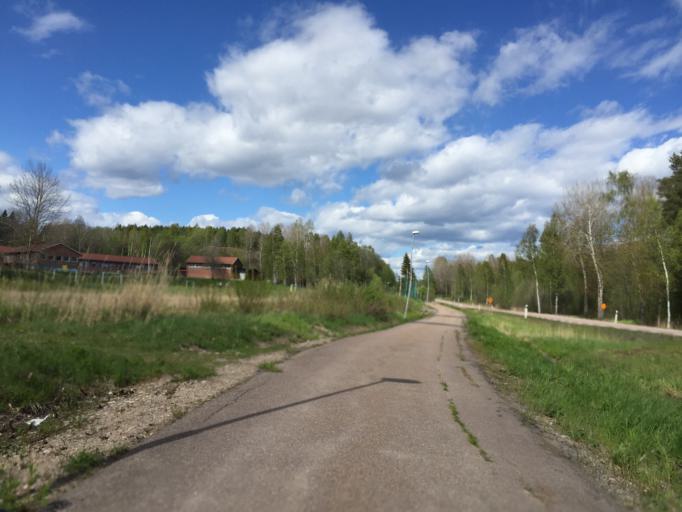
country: SE
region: Dalarna
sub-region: Ludvika Kommun
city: Ludvika
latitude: 60.1858
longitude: 15.2086
